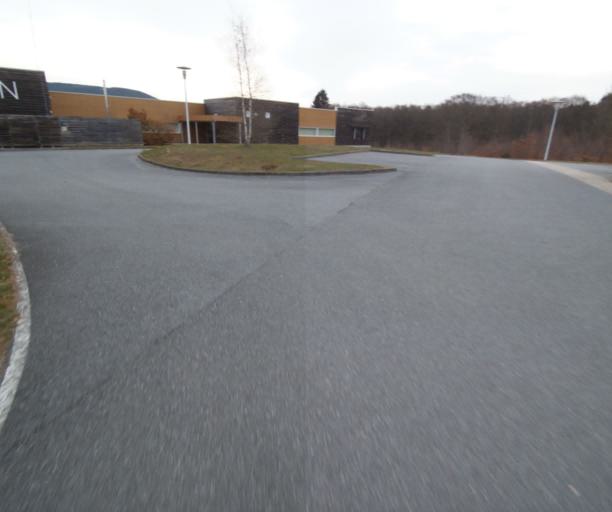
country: FR
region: Limousin
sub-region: Departement de la Correze
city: Correze
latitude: 45.4304
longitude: 1.8383
